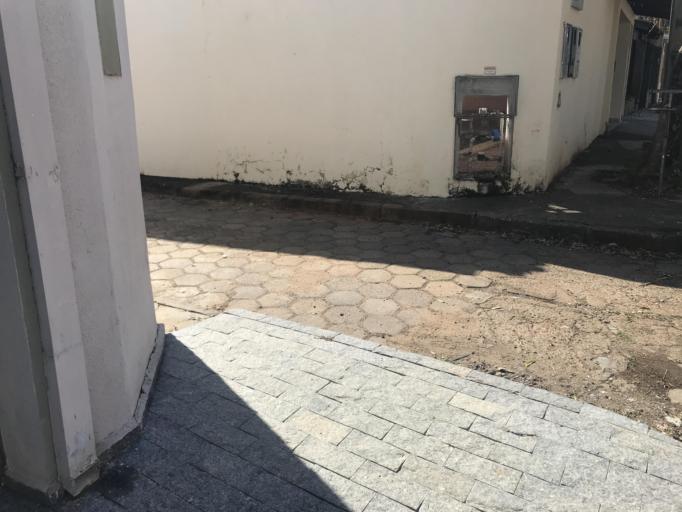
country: BR
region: Sao Paulo
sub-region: Presidente Prudente
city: Presidente Prudente
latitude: -22.1209
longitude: -51.4102
